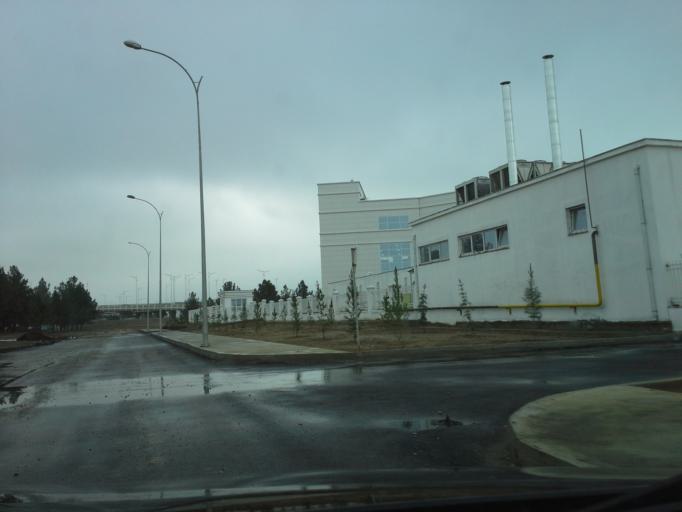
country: TM
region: Ahal
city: Ashgabat
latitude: 37.9634
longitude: 58.4167
